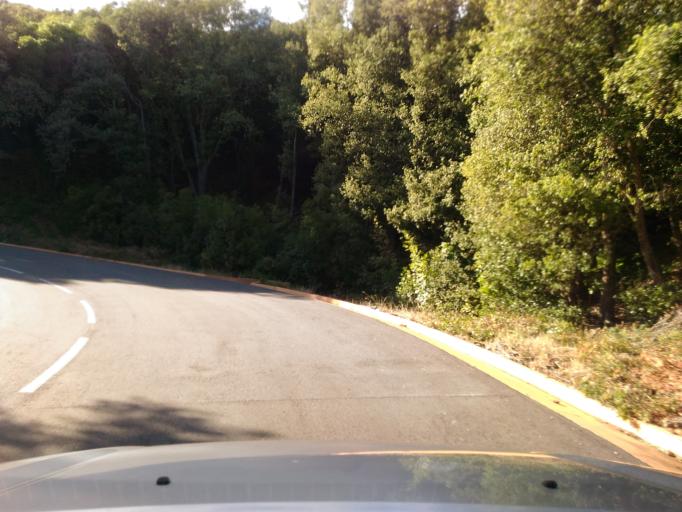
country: FR
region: Corsica
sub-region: Departement de la Haute-Corse
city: Brando
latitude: 42.9560
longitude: 9.4307
